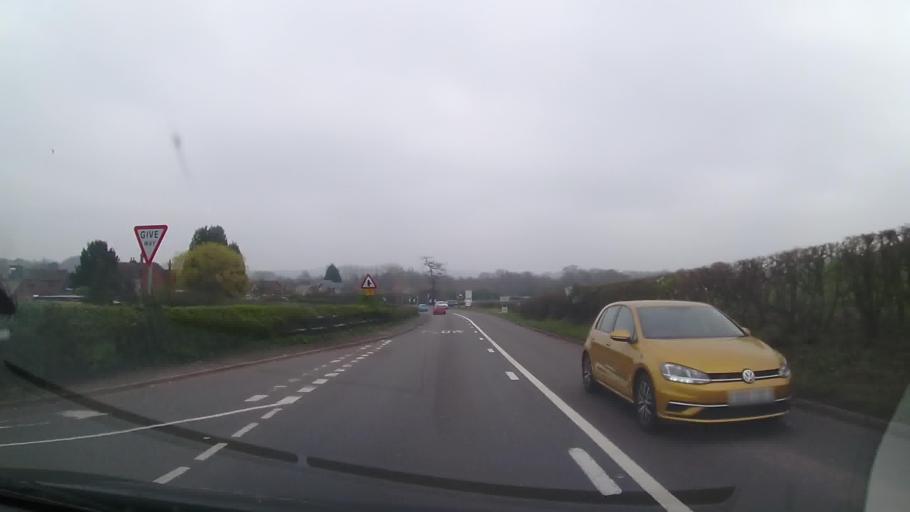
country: GB
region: England
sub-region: Staffordshire
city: Standon
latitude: 52.9561
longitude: -2.3138
